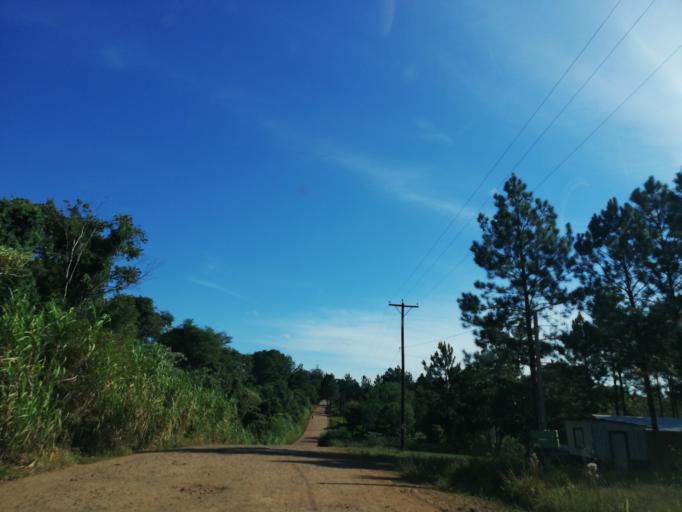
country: AR
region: Misiones
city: Dos de Mayo
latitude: -27.0154
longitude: -54.4528
